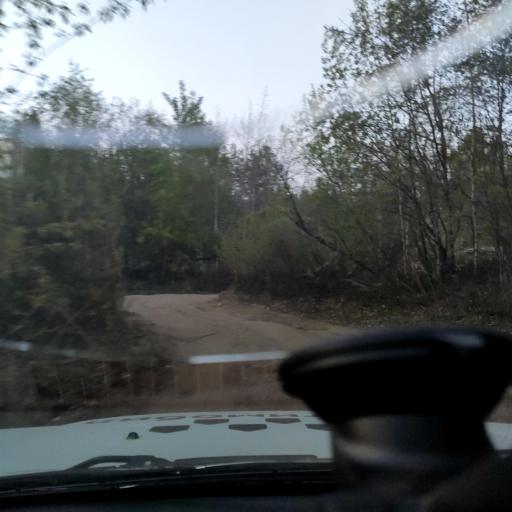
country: RU
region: Perm
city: Perm
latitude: 58.1119
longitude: 56.3392
